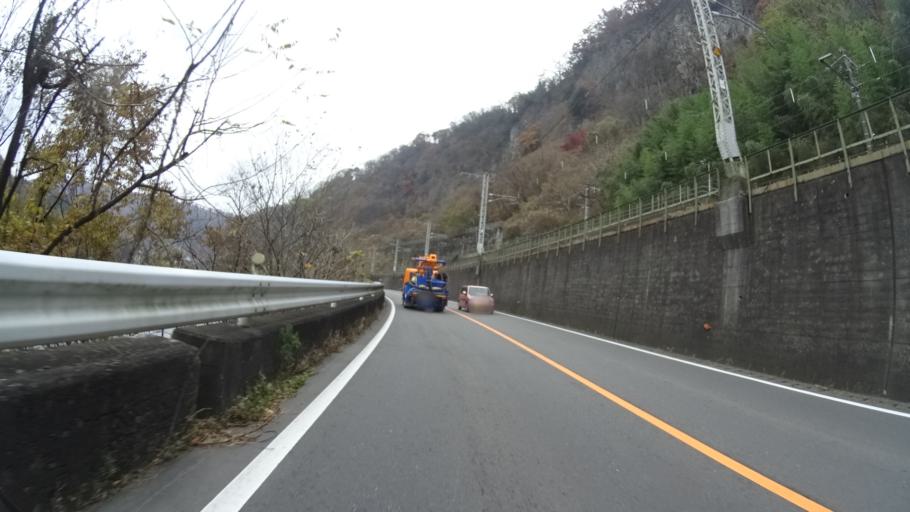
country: JP
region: Gunma
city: Numata
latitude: 36.5934
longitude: 139.0492
